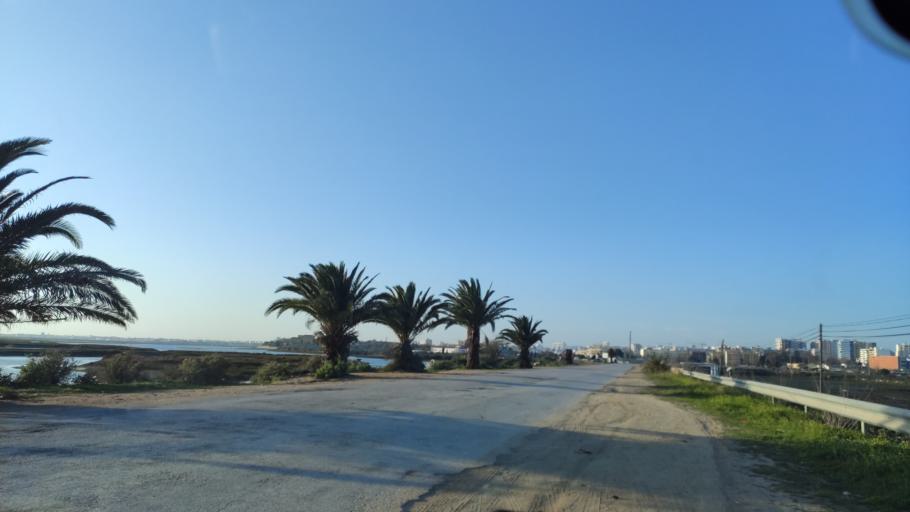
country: PT
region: Faro
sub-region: Faro
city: Faro
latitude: 37.0056
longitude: -7.9239
